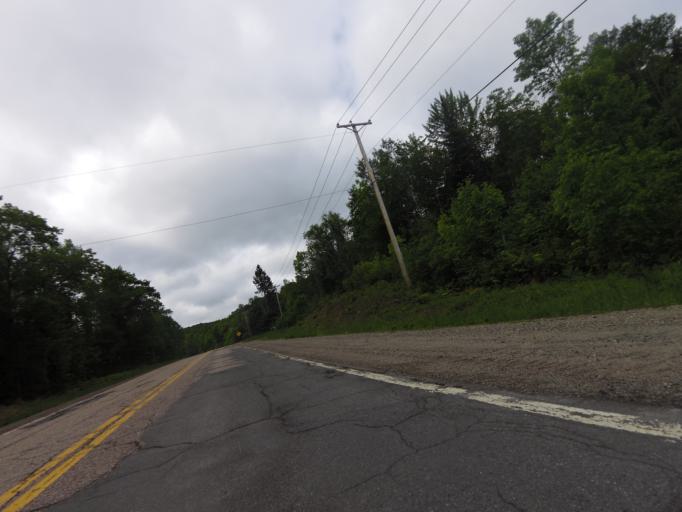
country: CA
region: Quebec
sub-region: Outaouais
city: Shawville
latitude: 45.8341
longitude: -76.4611
